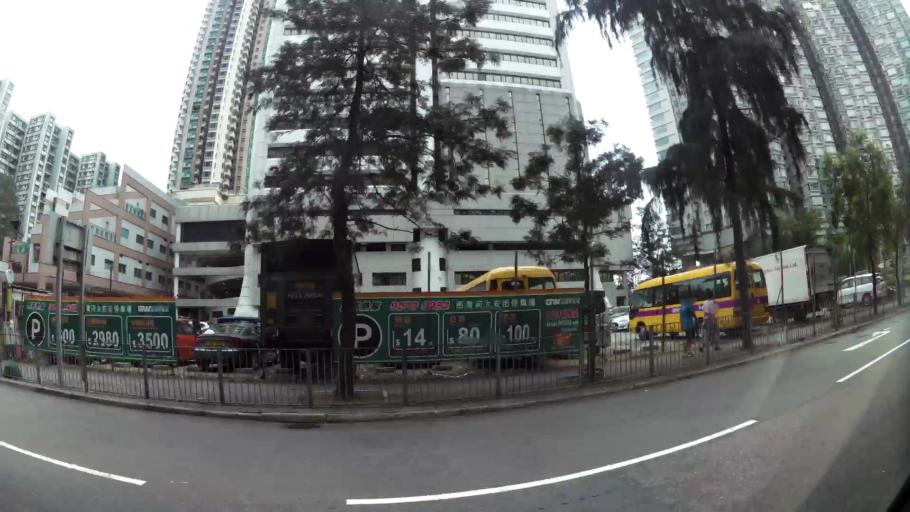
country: HK
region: Wanchai
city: Wan Chai
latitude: 22.2841
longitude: 114.2235
